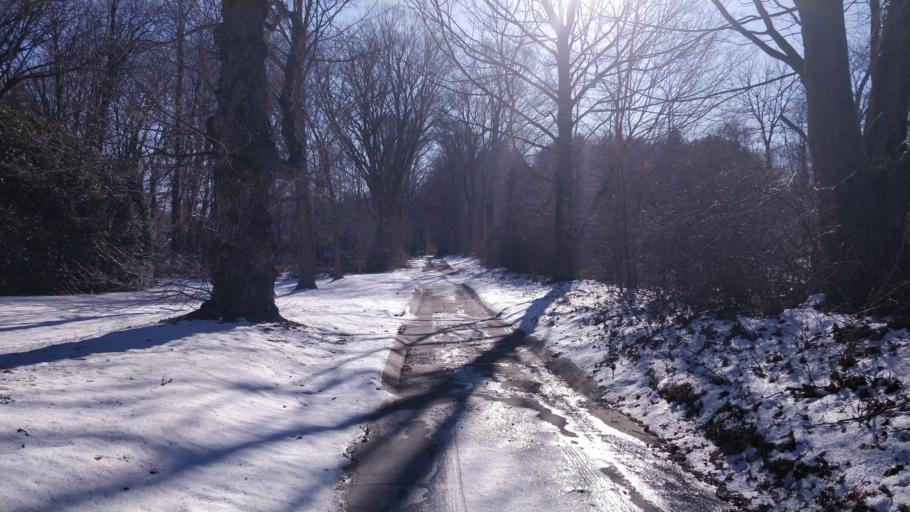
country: US
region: New York
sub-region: Nassau County
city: Brookville
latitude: 40.8103
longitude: -73.5844
